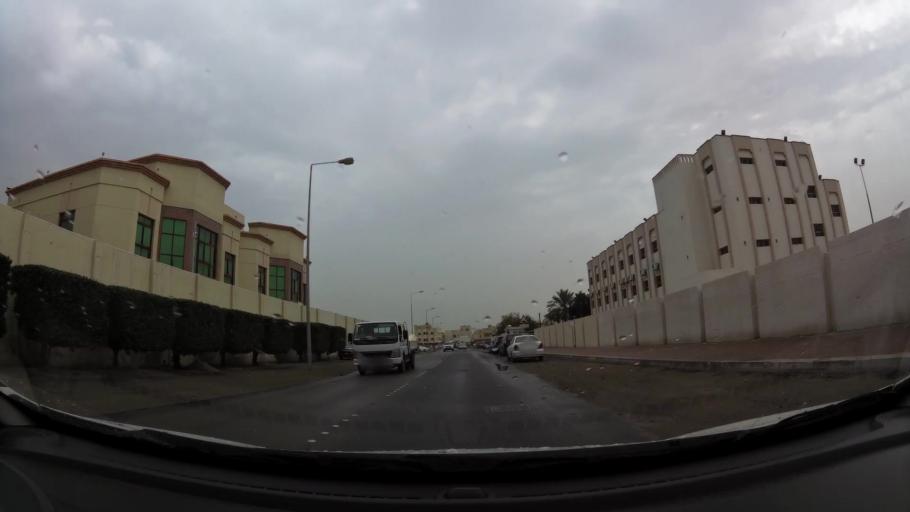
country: BH
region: Northern
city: Ar Rifa'
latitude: 26.1539
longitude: 50.5796
